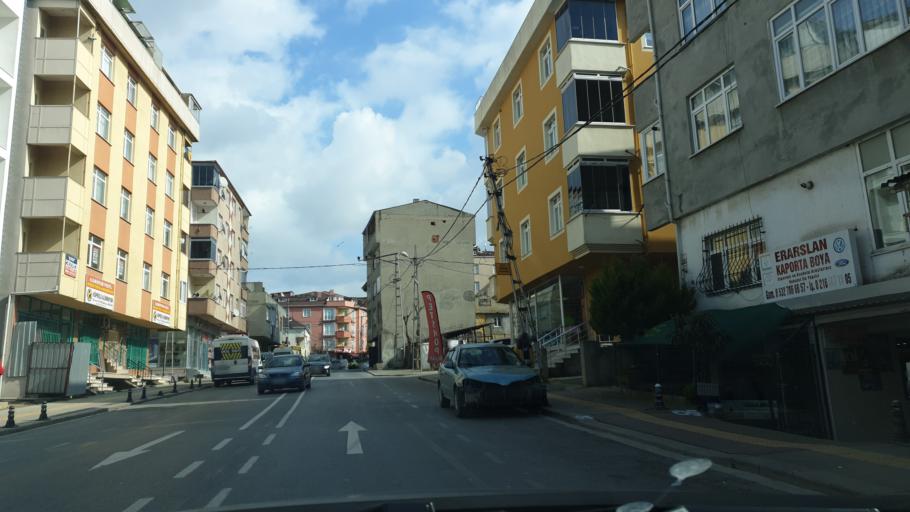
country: TR
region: Istanbul
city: Pendik
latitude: 40.8693
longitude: 29.2884
